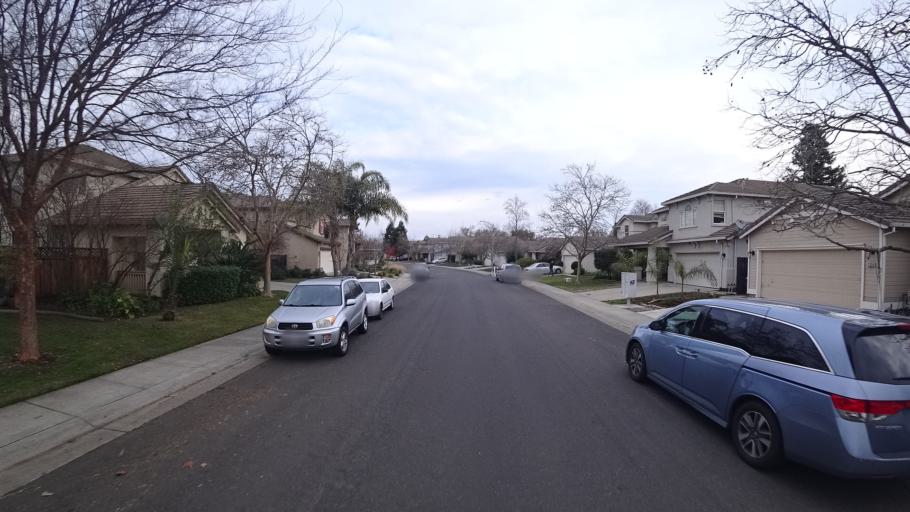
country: US
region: California
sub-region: Yolo County
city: Davis
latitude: 38.5660
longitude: -121.7248
